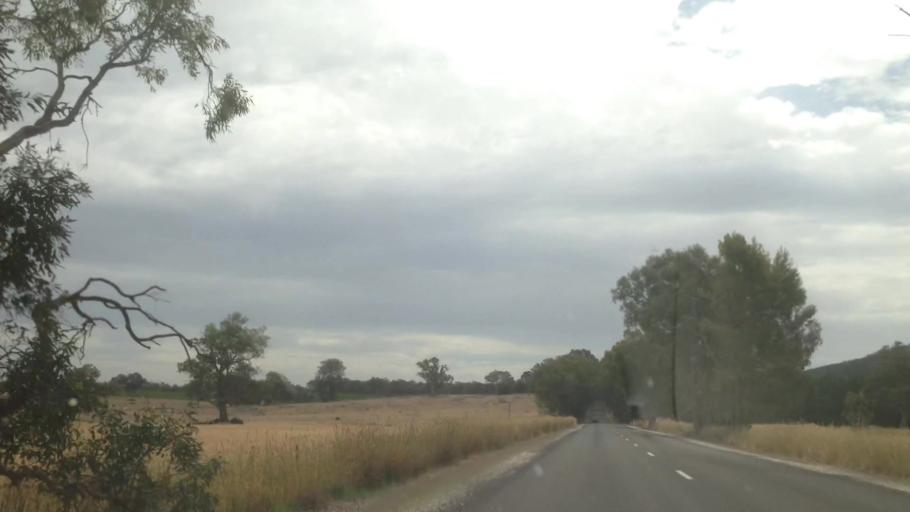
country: AU
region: South Australia
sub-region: Barossa
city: Williamstown
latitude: -34.6892
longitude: 138.9856
